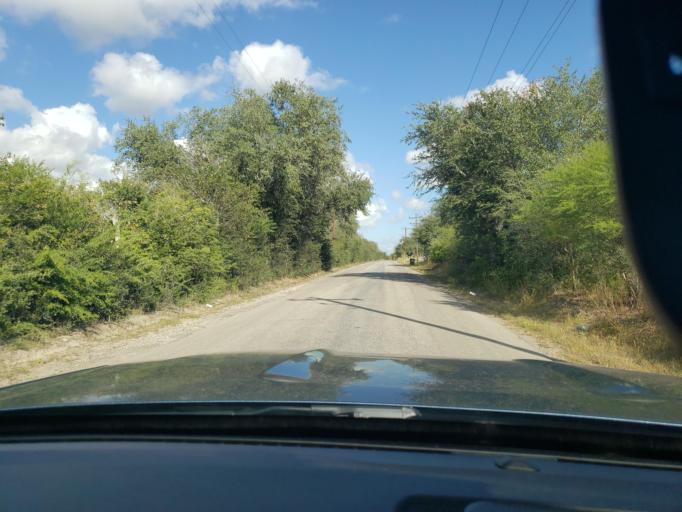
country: US
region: Texas
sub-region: Bee County
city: Beeville
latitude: 28.4439
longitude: -97.7148
